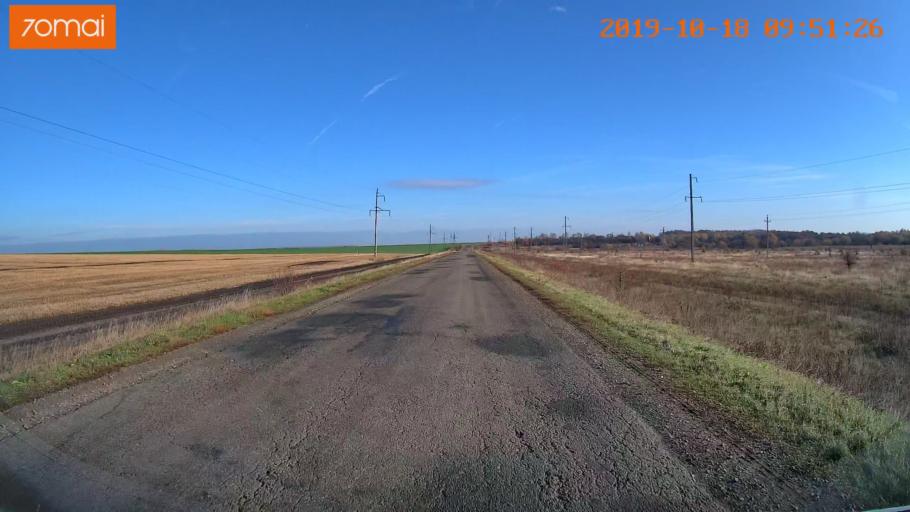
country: RU
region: Tula
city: Kazachka
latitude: 53.3406
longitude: 38.2925
